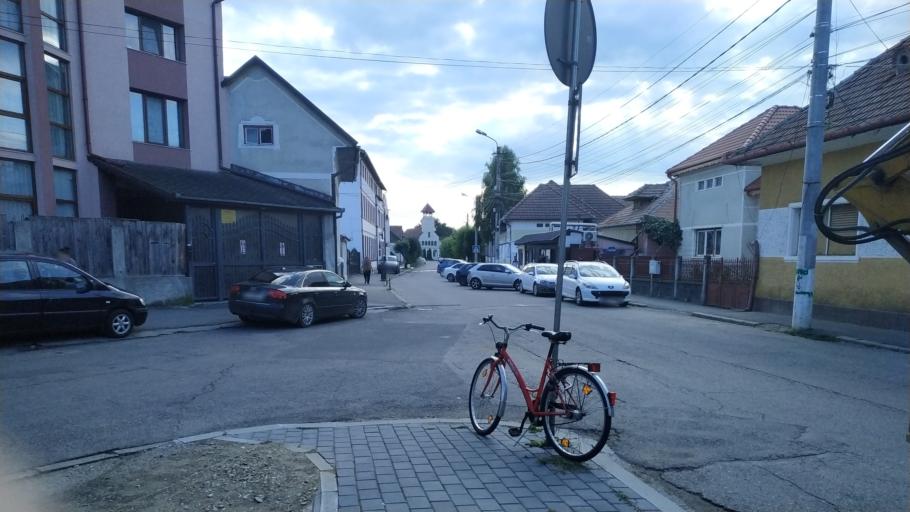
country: RO
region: Brasov
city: Fogarasch
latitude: 45.8423
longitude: 24.9687
